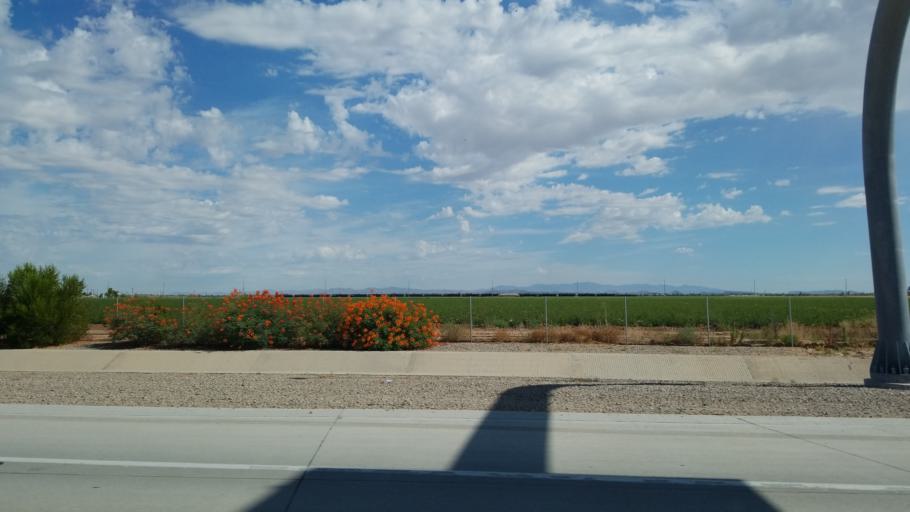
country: US
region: Arizona
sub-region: Maricopa County
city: Citrus Park
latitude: 33.5593
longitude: -112.3887
